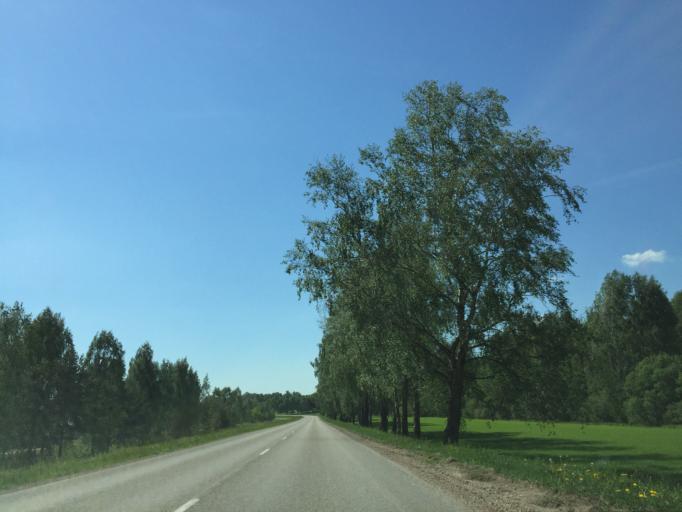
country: LV
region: Bauskas Rajons
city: Bauska
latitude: 56.4269
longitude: 24.2834
